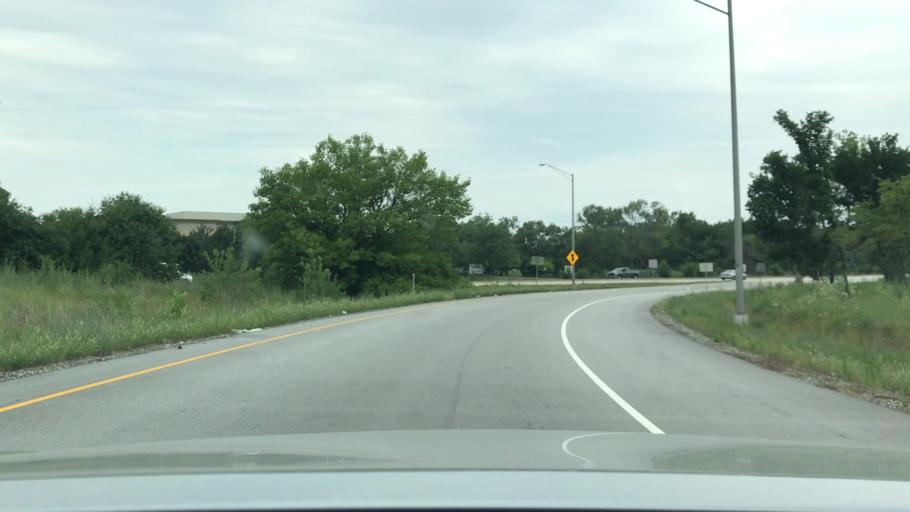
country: US
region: Illinois
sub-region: Cook County
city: Lemont
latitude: 41.7188
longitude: -88.0061
